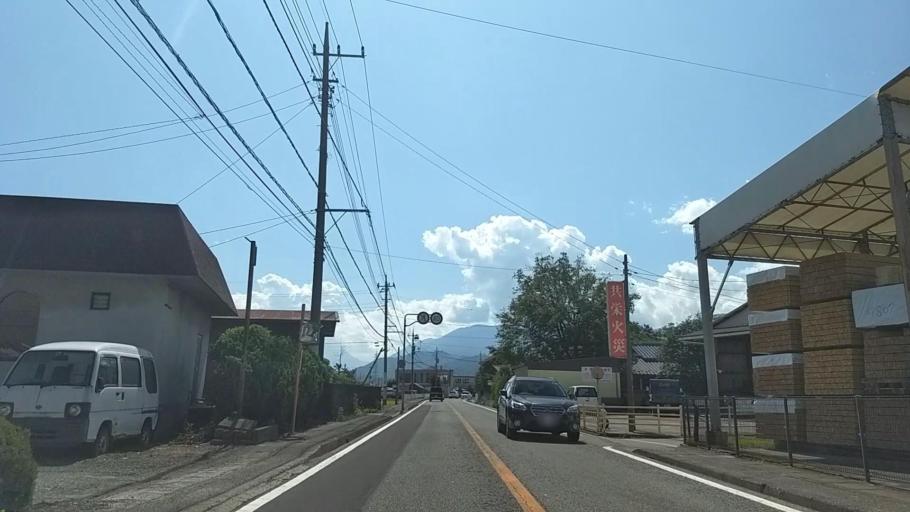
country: JP
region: Yamanashi
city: Ryuo
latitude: 35.5771
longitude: 138.4894
